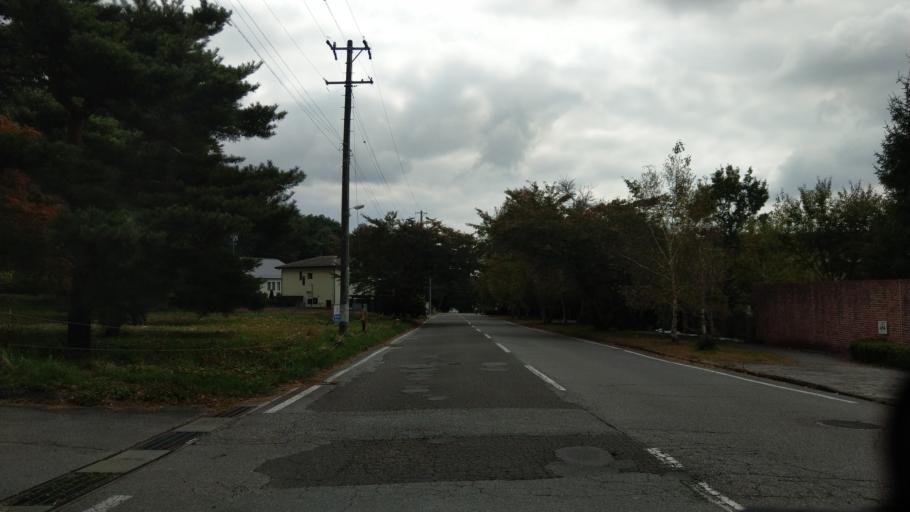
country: JP
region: Nagano
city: Komoro
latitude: 36.3301
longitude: 138.5240
